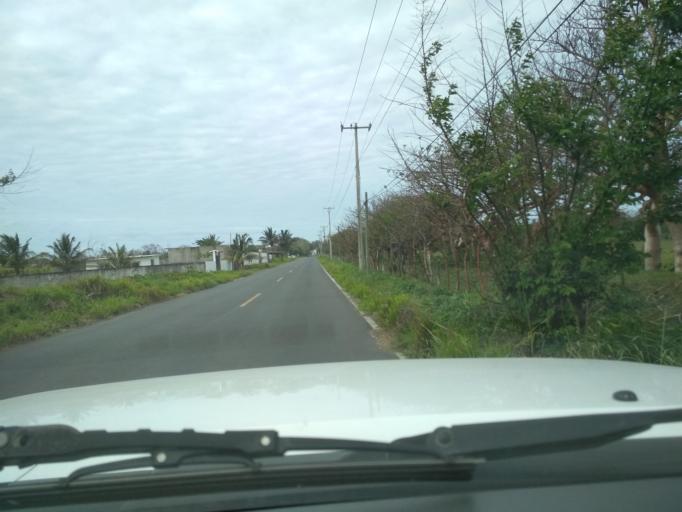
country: MX
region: Veracruz
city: Anton Lizardo
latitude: 19.0492
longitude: -95.9865
